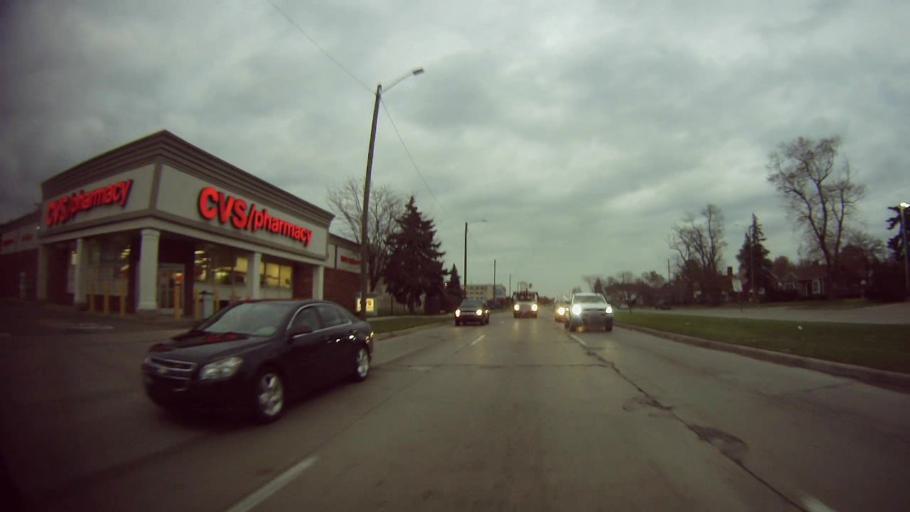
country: US
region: Michigan
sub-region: Macomb County
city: Warren
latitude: 42.4413
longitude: -83.0241
